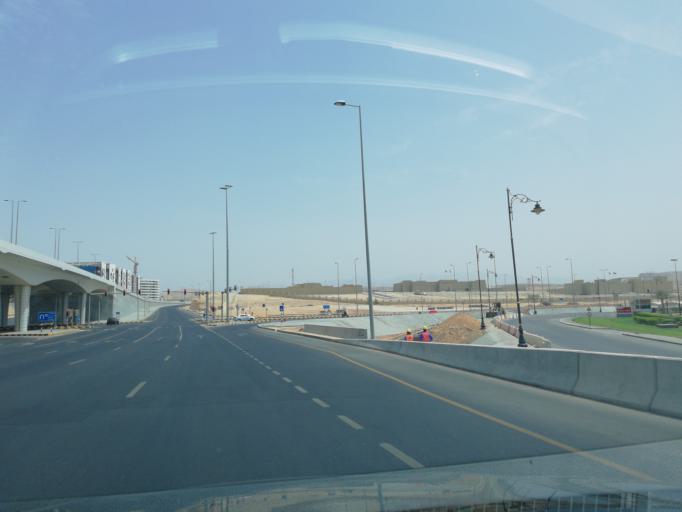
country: OM
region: Muhafazat Masqat
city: Bawshar
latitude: 23.5790
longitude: 58.2943
